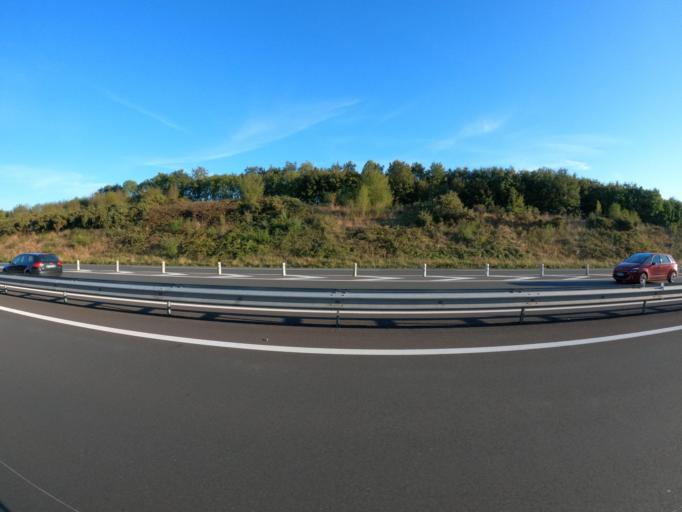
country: FR
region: Pays de la Loire
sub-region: Departement de la Vendee
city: Saint-Fulgent
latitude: 46.8118
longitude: -1.2006
